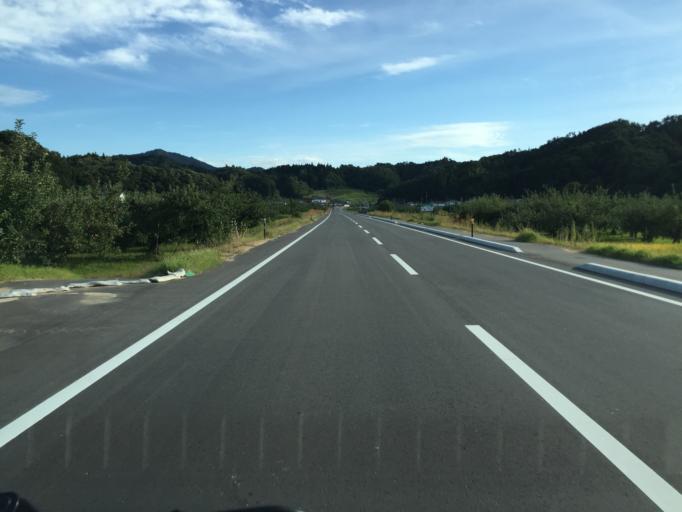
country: JP
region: Fukushima
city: Hobaramachi
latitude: 37.7479
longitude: 140.6072
